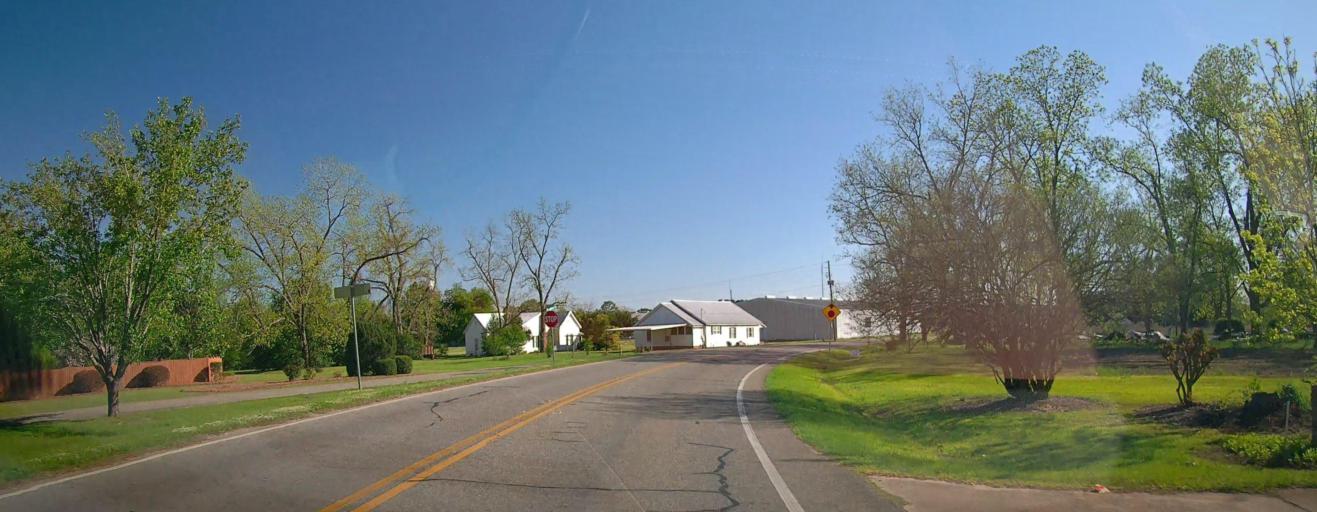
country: US
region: Georgia
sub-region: Wilcox County
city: Rochelle
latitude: 31.8106
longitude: -83.4890
